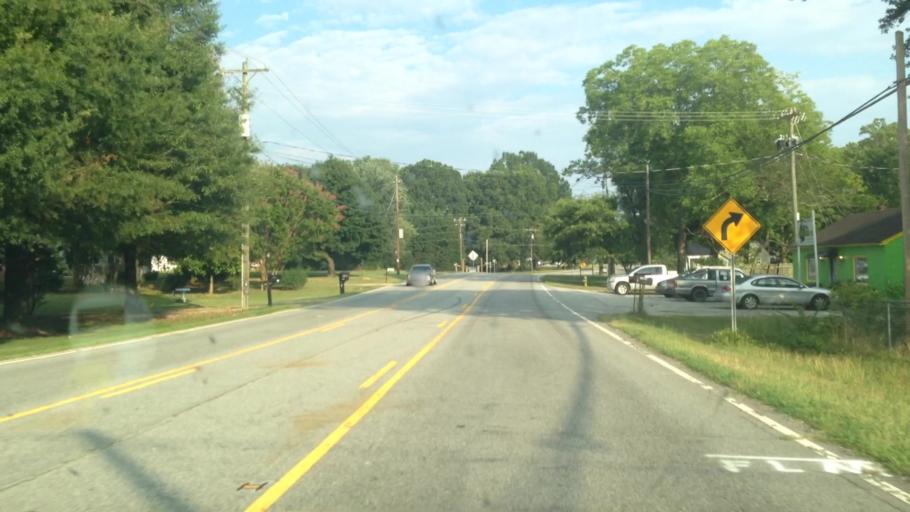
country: US
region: North Carolina
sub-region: Forsyth County
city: Kernersville
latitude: 36.0415
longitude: -80.0523
